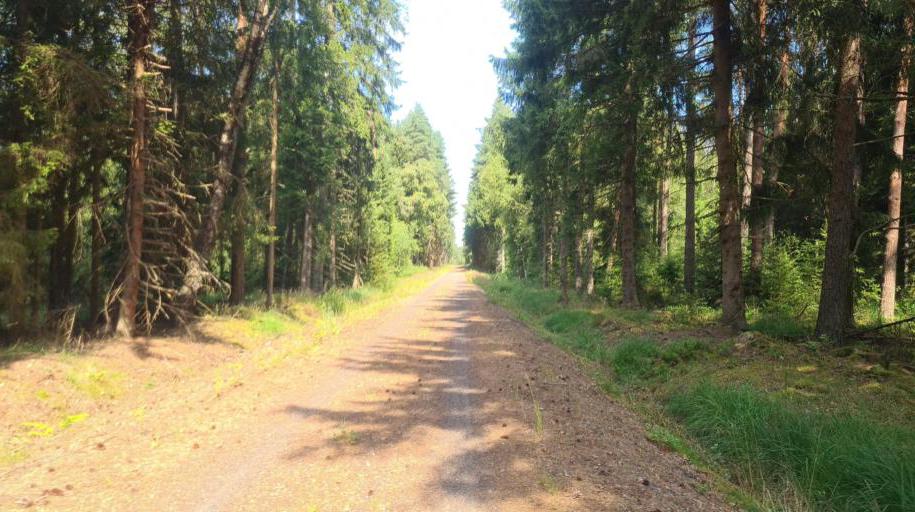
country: SE
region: Kronoberg
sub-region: Ljungby Kommun
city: Lagan
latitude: 56.9507
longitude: 13.9622
